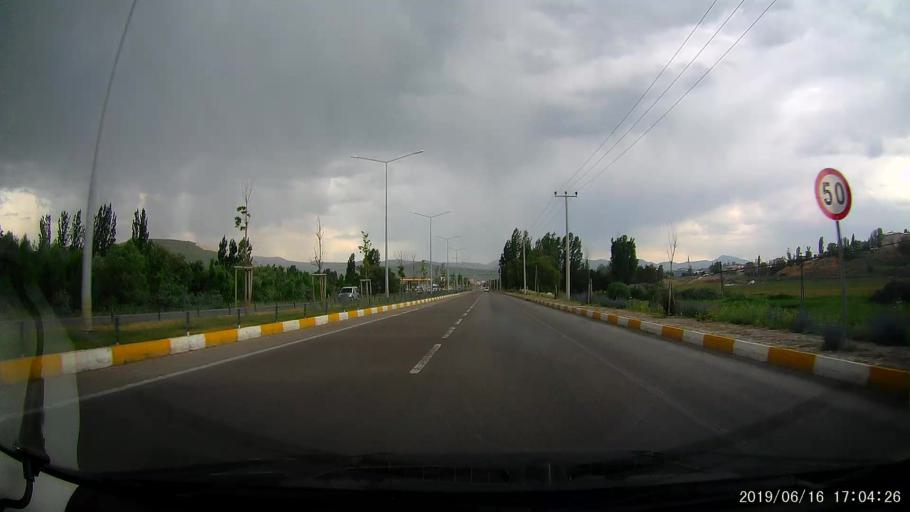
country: TR
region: Erzurum
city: Askale
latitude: 39.9260
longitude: 40.7092
